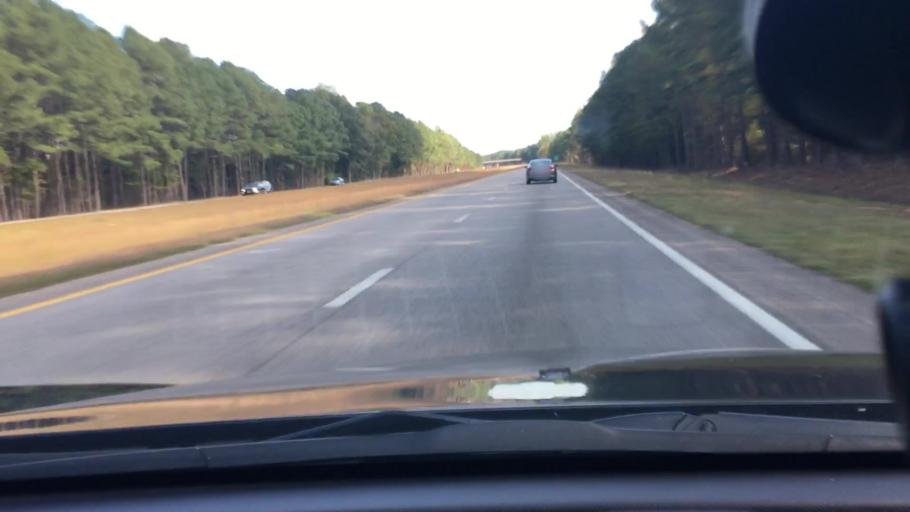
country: US
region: North Carolina
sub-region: Wilson County
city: Lucama
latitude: 35.7815
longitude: -78.0857
